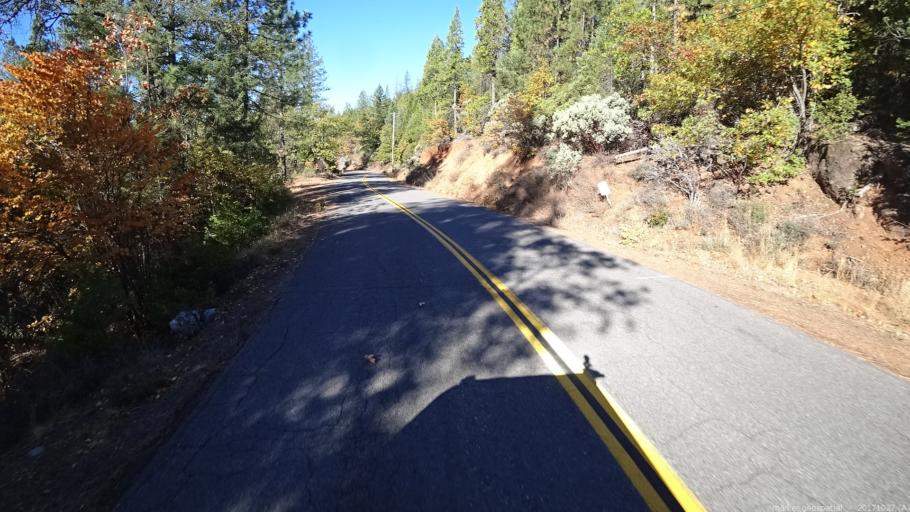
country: US
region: California
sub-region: Shasta County
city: Bella Vista
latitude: 40.8175
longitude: -121.9772
